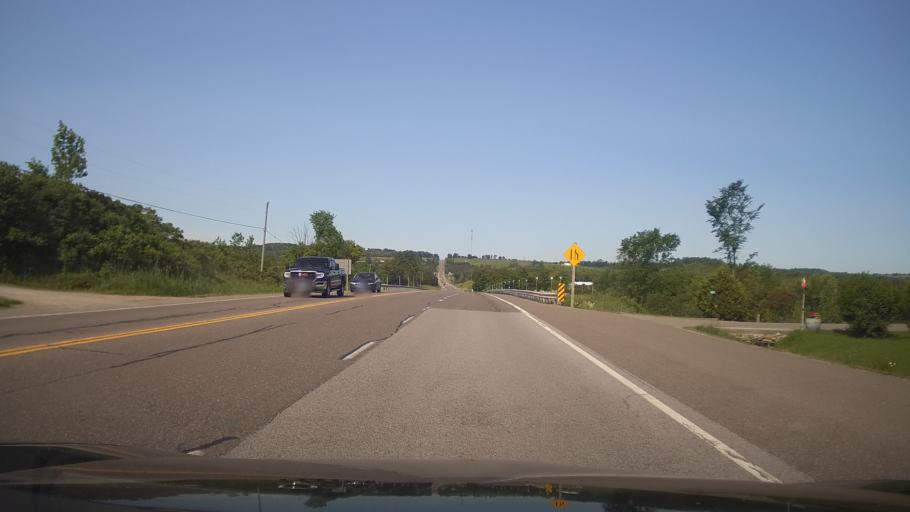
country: CA
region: Ontario
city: Omemee
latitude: 44.3238
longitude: -78.4581
